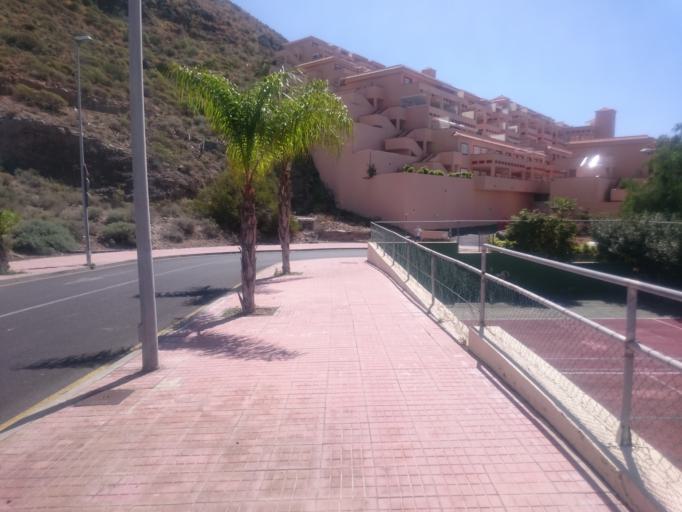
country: ES
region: Canary Islands
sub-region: Provincia de Santa Cruz de Tenerife
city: Playa de las Americas
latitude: 28.0558
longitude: -16.7033
